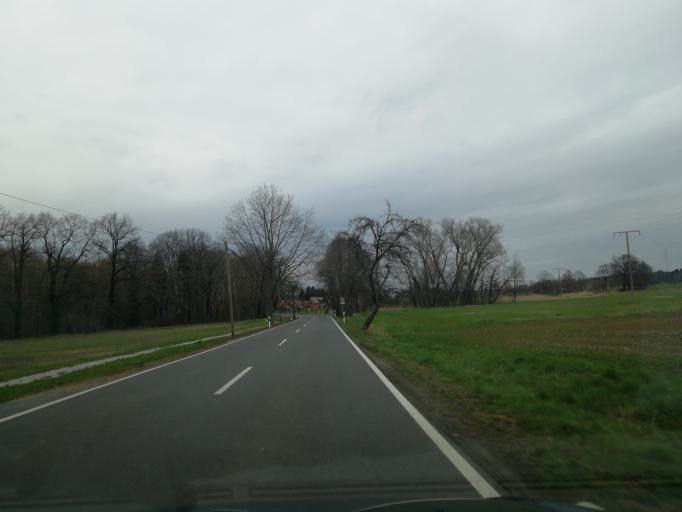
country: DE
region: Brandenburg
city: Vetschau
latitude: 51.7560
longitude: 14.0543
